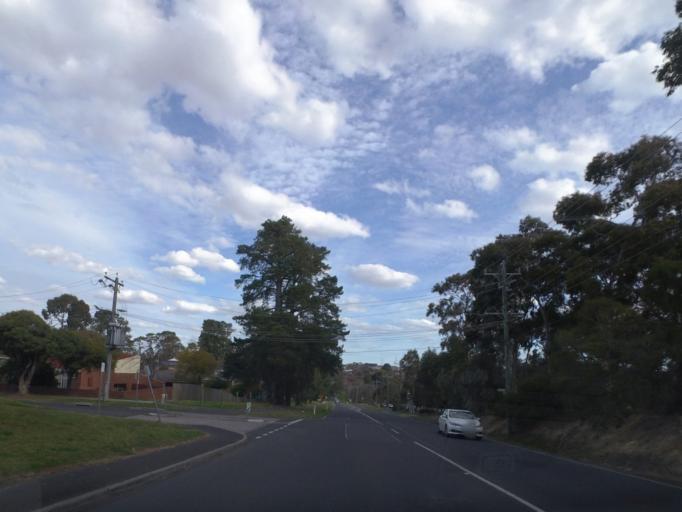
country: AU
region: Victoria
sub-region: Manningham
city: Doncaster East
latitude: -37.7759
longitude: 145.1456
